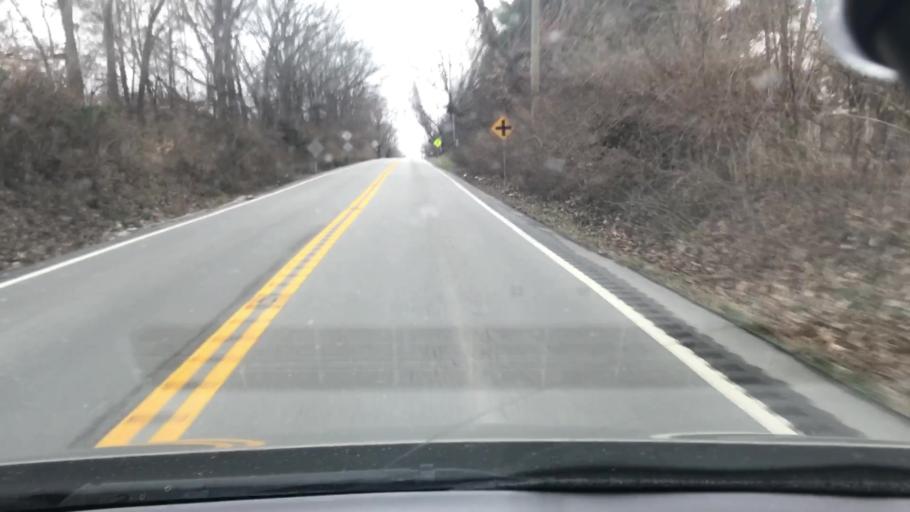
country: US
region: Kentucky
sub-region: Jefferson County
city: Barbourmeade
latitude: 38.2915
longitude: -85.6144
